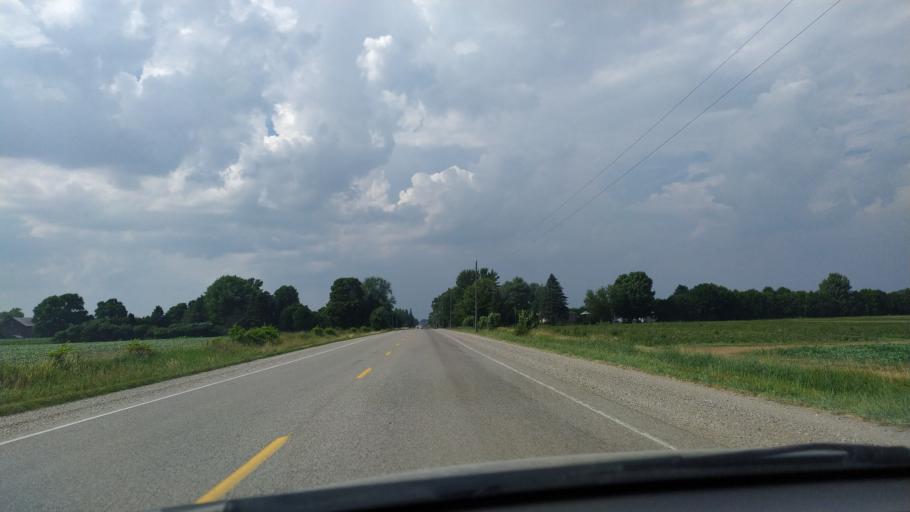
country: CA
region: Ontario
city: Dorchester
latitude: 43.0358
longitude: -81.1233
